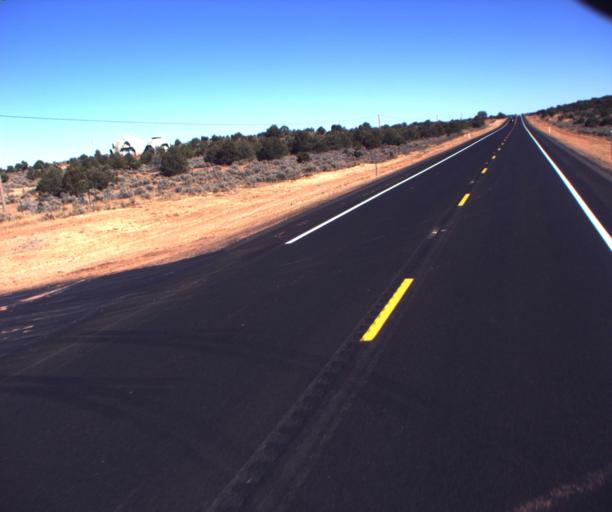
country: US
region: Arizona
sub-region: Apache County
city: Ganado
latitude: 35.7164
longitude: -109.4215
